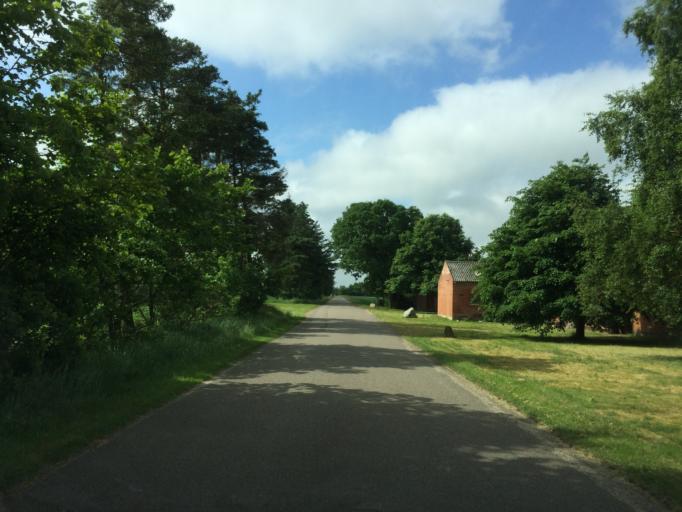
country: DK
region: Central Jutland
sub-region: Holstebro Kommune
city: Ulfborg
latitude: 56.2300
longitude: 8.4369
